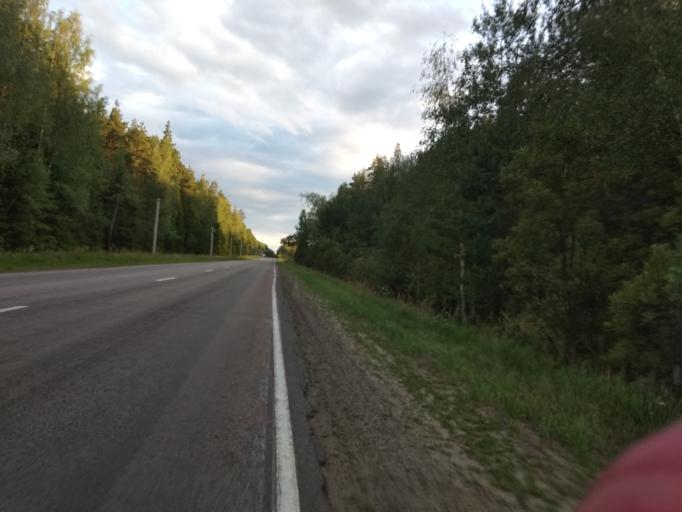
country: RU
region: Moskovskaya
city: Misheronskiy
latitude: 55.6226
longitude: 39.7312
